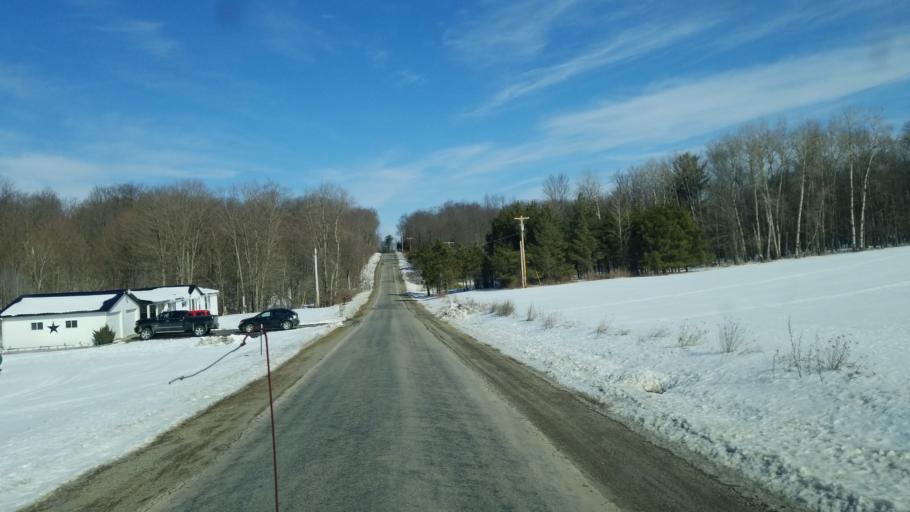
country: US
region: New York
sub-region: Allegany County
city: Andover
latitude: 42.0823
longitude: -77.7716
